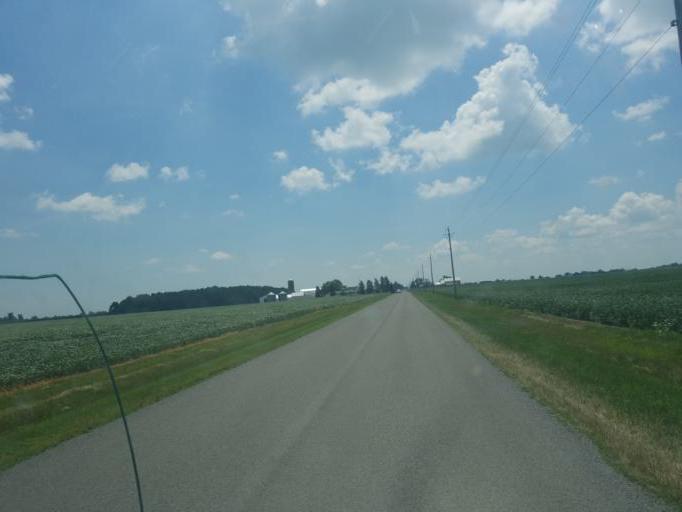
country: US
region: Ohio
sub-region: Mercer County
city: Celina
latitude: 40.5667
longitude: -84.4939
